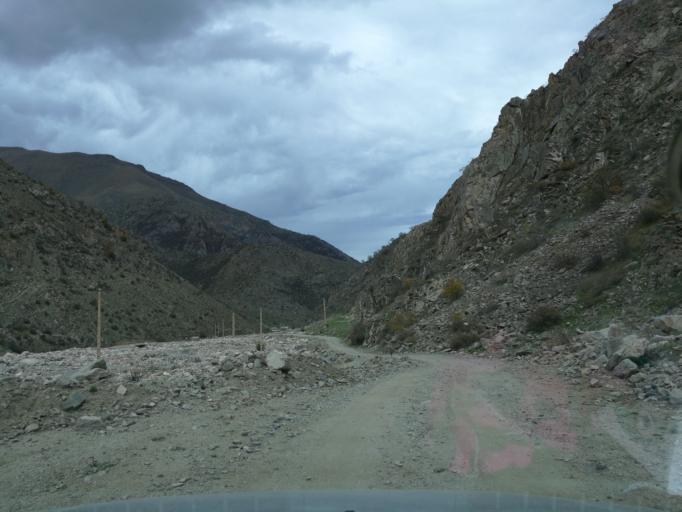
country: IR
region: Mazandaran
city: `Abbasabad
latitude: 36.4294
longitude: 51.0408
